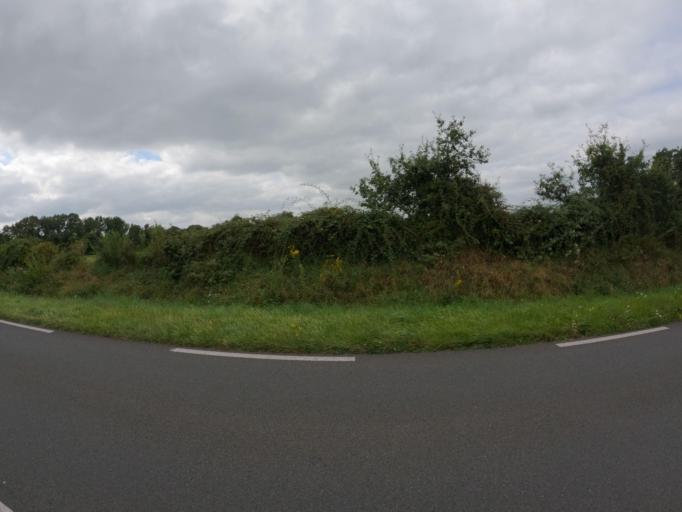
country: FR
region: Poitou-Charentes
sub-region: Departement de la Charente
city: Etagnac
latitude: 45.9035
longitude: 0.7634
